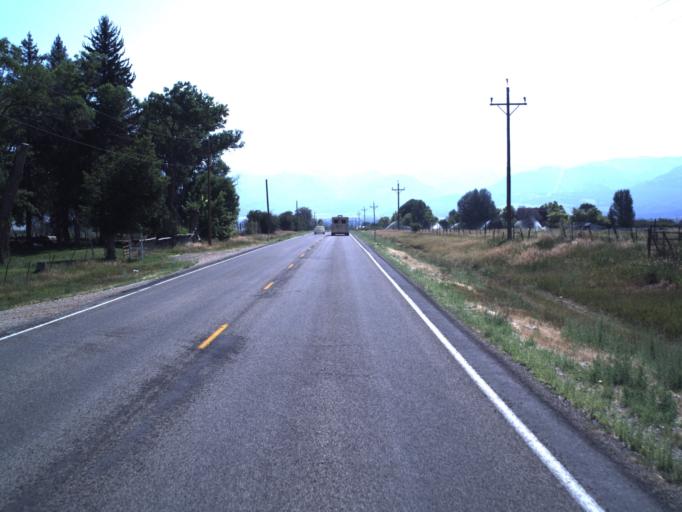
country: US
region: Utah
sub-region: Sanpete County
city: Mount Pleasant
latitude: 39.5467
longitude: -111.5089
